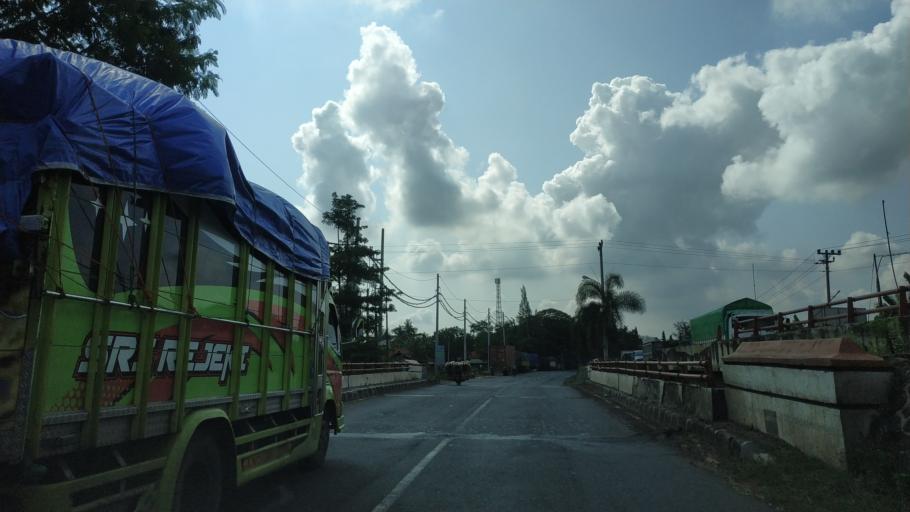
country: ID
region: Central Java
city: Wiradesa
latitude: -6.8883
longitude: 109.5822
